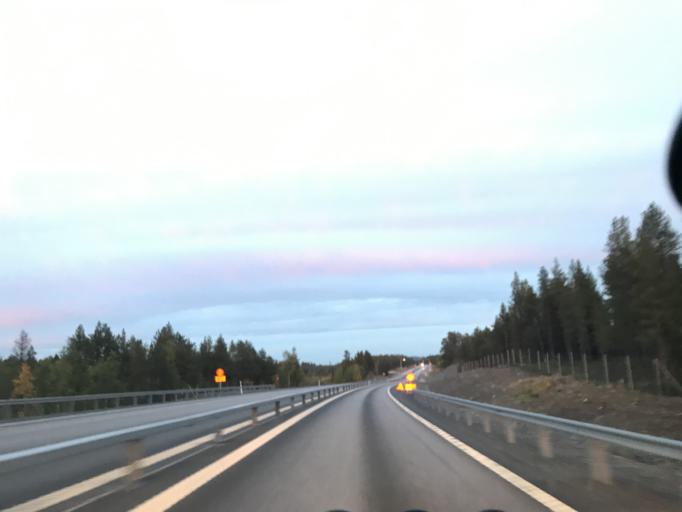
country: SE
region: Norrbotten
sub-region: Gallivare Kommun
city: Malmberget
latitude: 67.6716
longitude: 20.9432
